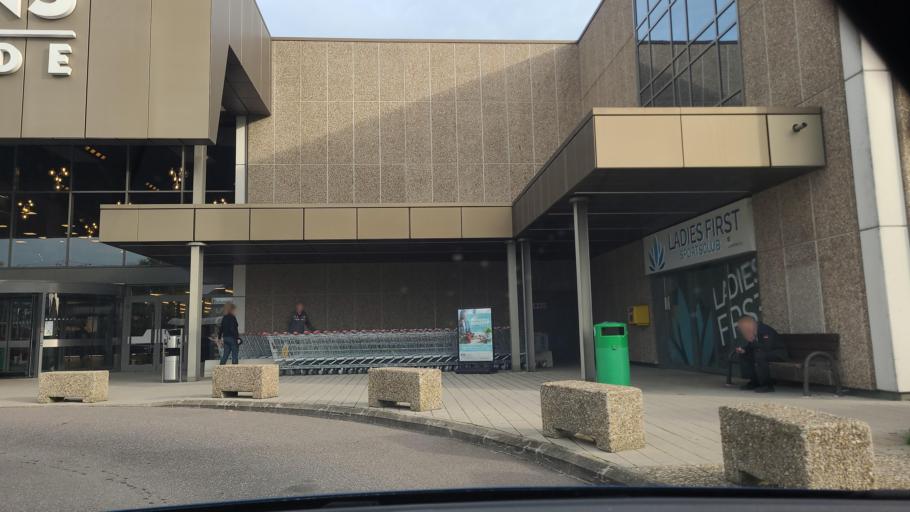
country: LU
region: Luxembourg
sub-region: Canton de Luxembourg
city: Bertrange
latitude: 49.6226
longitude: 6.0533
